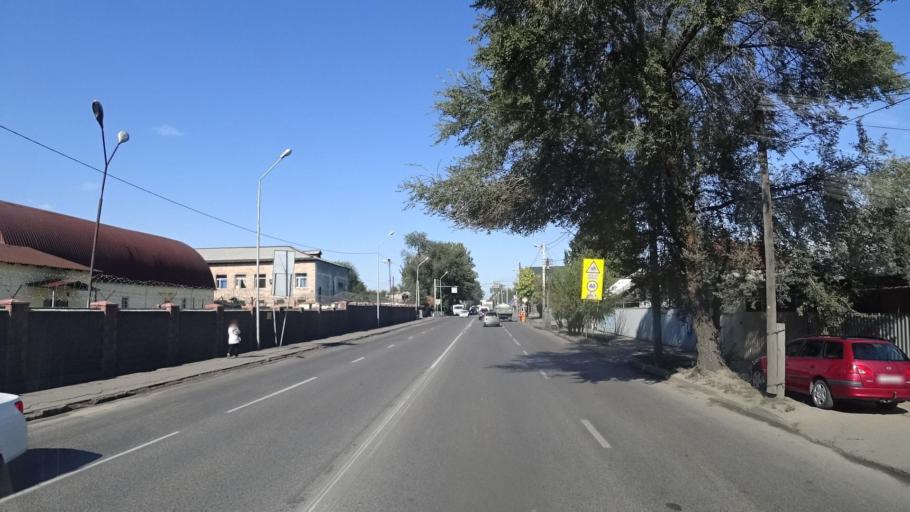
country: KZ
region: Almaty Oblysy
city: Pervomayskiy
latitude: 43.3520
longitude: 76.9579
